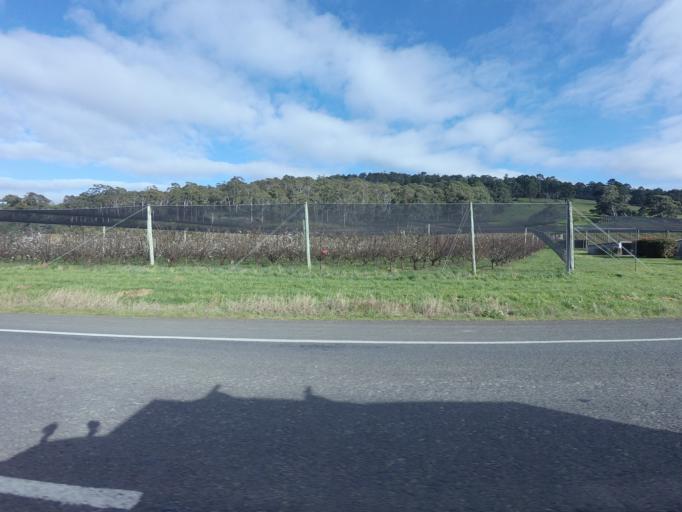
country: AU
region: Tasmania
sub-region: Huon Valley
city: Huonville
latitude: -43.0500
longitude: 147.0386
